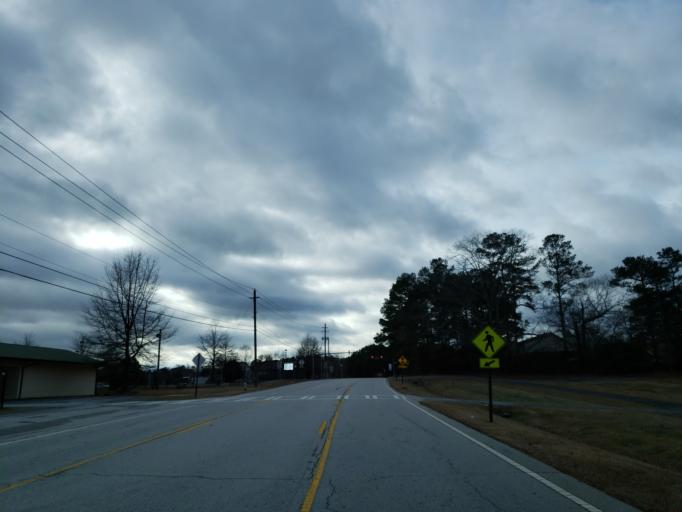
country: US
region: Georgia
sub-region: Cobb County
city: Fair Oaks
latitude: 33.9021
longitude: -84.5919
